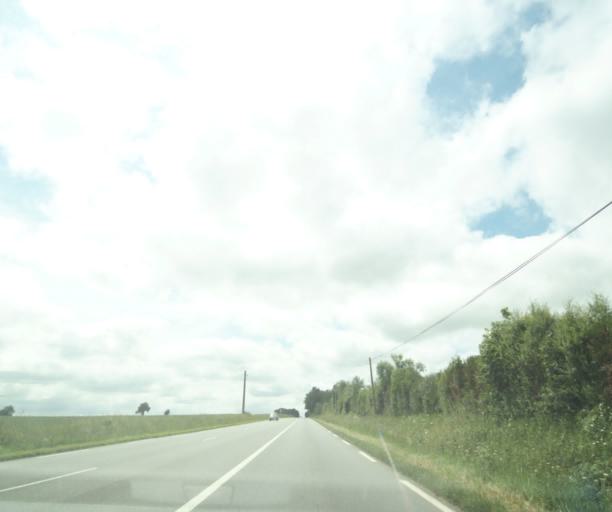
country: FR
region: Poitou-Charentes
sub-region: Departement des Deux-Sevres
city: Le Tallud
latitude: 46.6164
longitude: -0.2832
